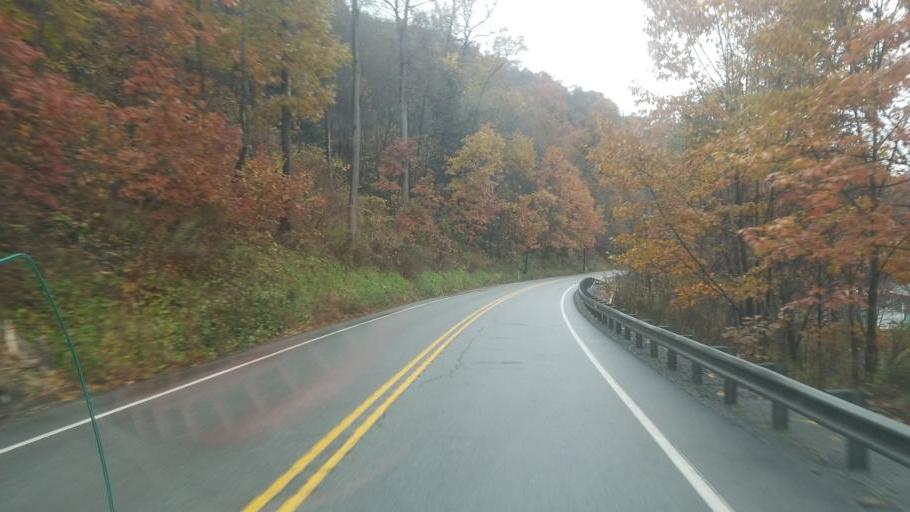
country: US
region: Pennsylvania
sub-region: Clearfield County
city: Clearfield
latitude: 41.0568
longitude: -78.3786
